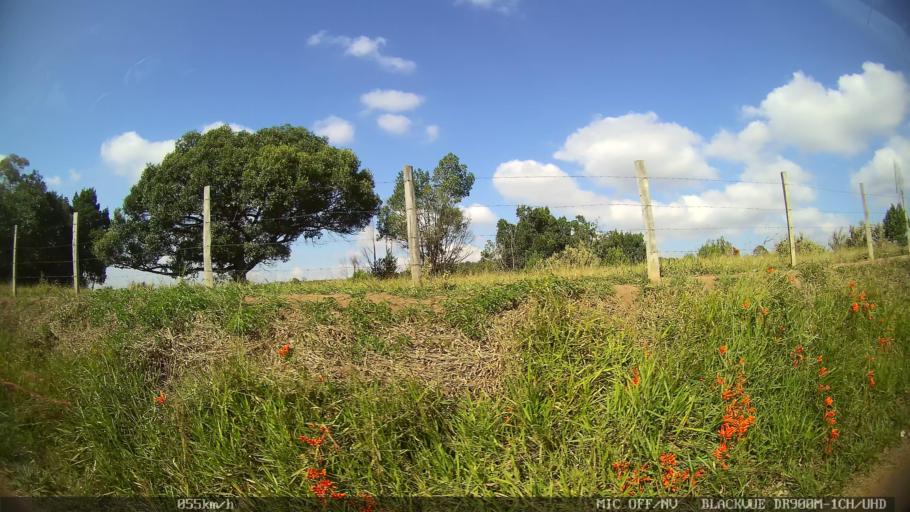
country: BR
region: Sao Paulo
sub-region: Indaiatuba
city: Indaiatuba
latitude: -22.9977
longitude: -47.2001
